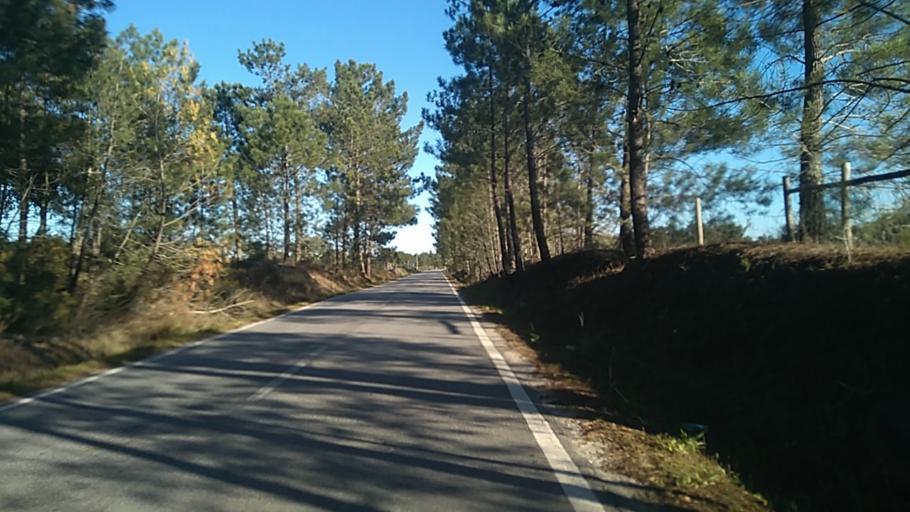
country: PT
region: Evora
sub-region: Vendas Novas
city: Vendas Novas
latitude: 38.8089
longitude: -8.4246
